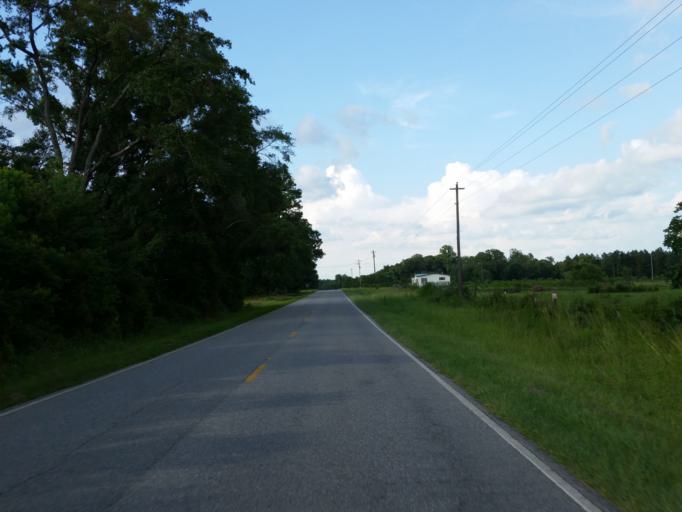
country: US
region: Georgia
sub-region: Crisp County
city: Cordele
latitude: 32.0197
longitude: -83.8463
